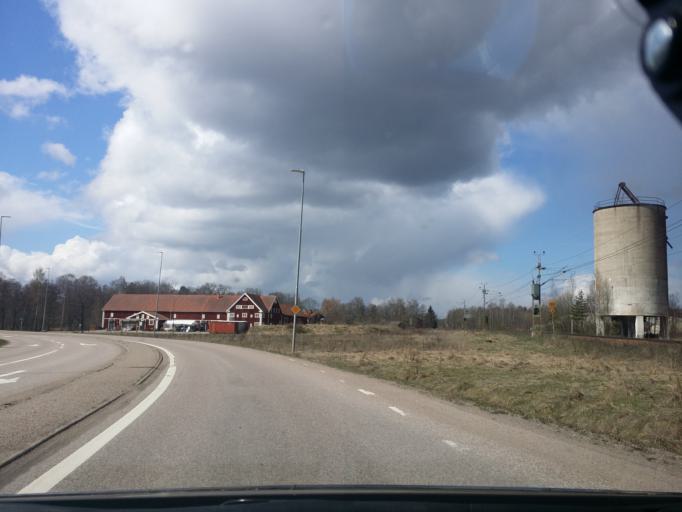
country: SE
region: Vaestmanland
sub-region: Sala Kommun
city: Sala
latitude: 59.9287
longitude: 16.5943
